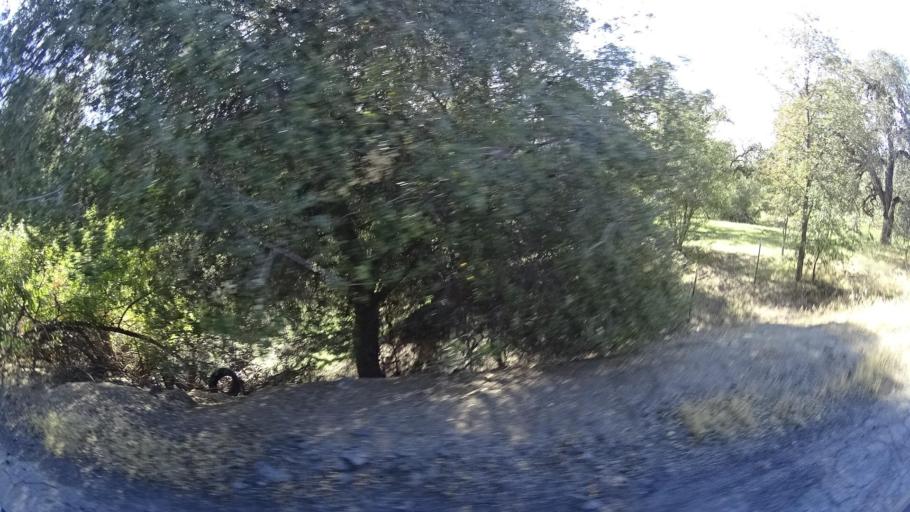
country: US
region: California
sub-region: Kern County
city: Alta Sierra
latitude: 35.6305
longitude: -118.7931
